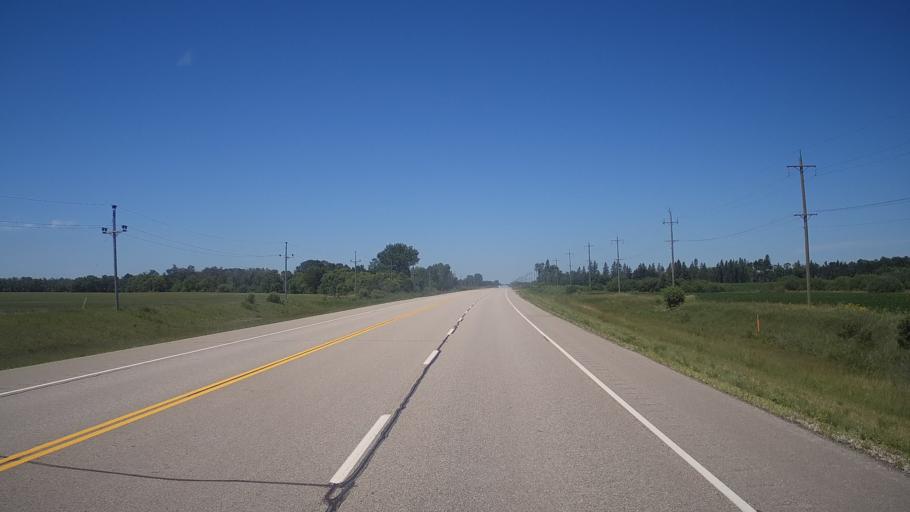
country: CA
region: Manitoba
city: Neepawa
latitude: 50.2253
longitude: -99.2758
